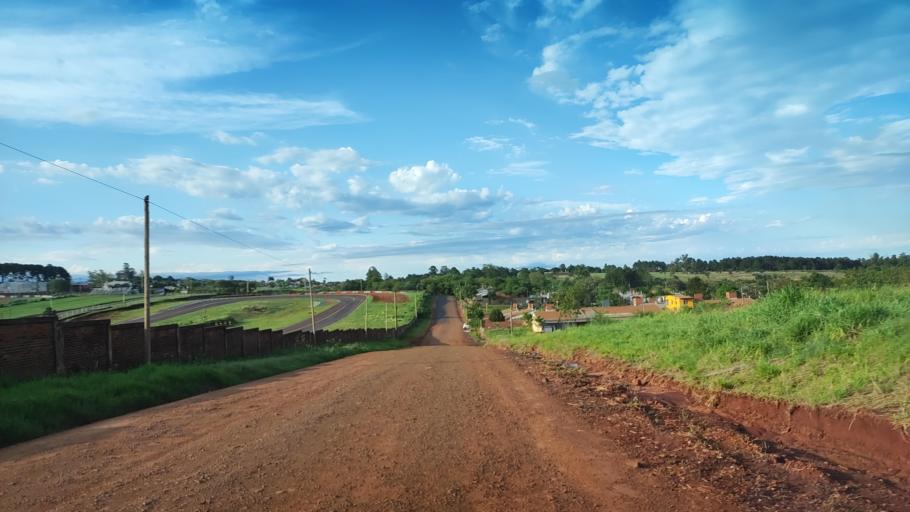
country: AR
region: Misiones
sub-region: Departamento de Capital
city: Posadas
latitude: -27.4387
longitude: -55.9242
